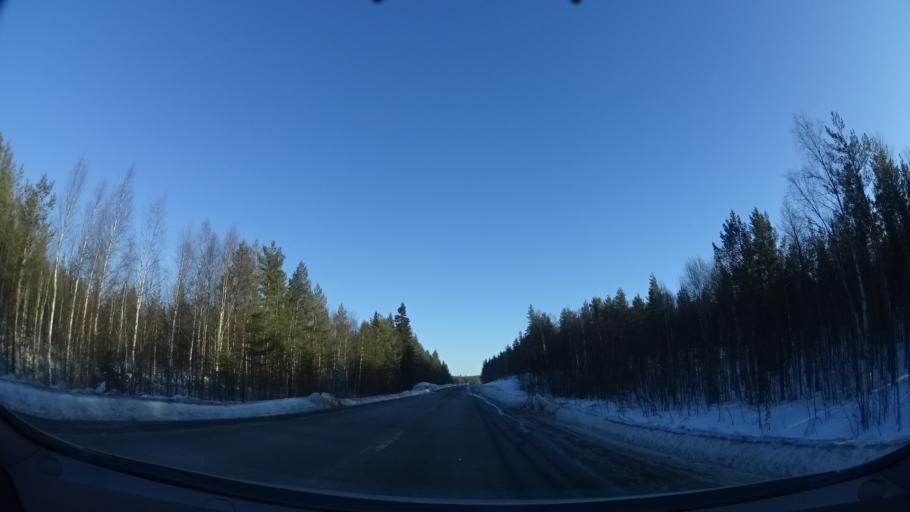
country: SE
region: Vaesterbotten
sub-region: Skelleftea Kommun
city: Langsele
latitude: 65.0476
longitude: 20.0693
